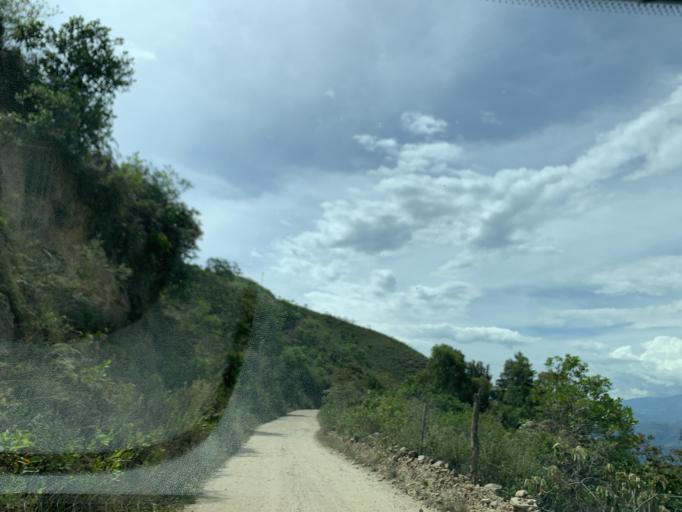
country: CO
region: Boyaca
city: Tipacoque
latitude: 6.4467
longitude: -72.7062
